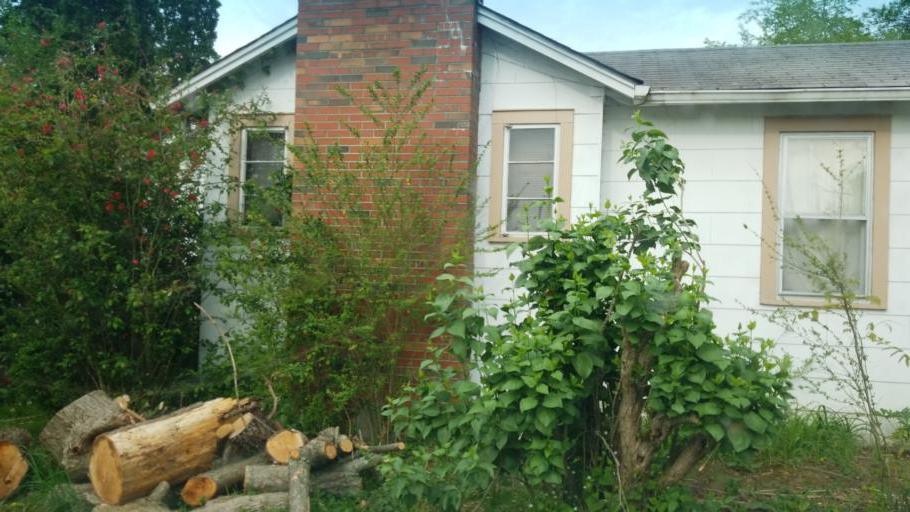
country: US
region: Virginia
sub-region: Smyth County
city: Marion
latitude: 36.8415
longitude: -81.5243
